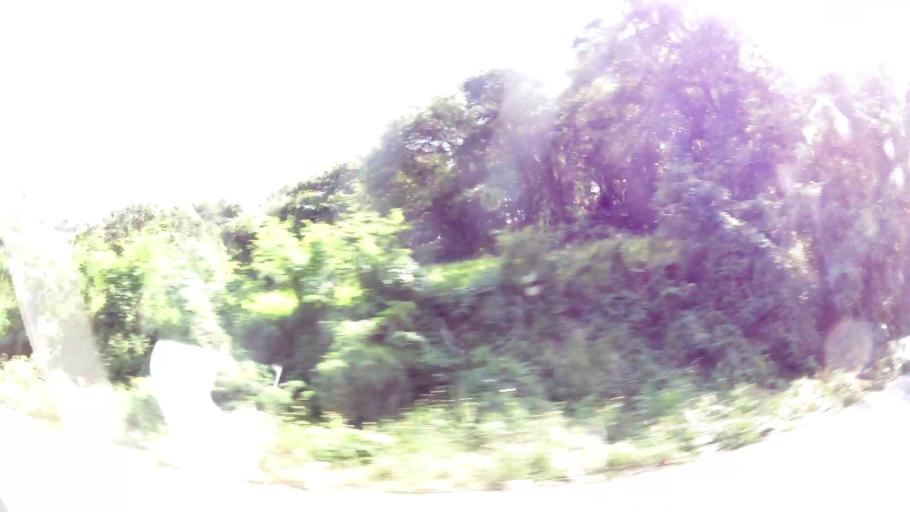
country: DO
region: San Cristobal
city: Bajos de Haina
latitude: 18.4262
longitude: -70.0555
